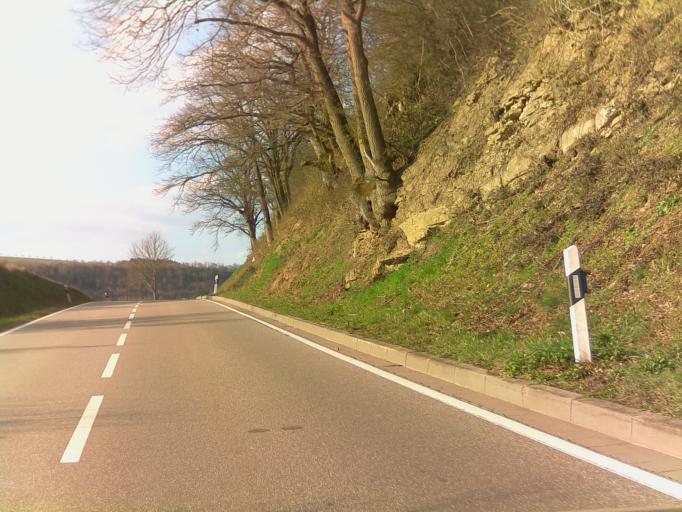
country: DE
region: Rheinland-Pfalz
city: Meisenheim
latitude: 49.7173
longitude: 7.6702
